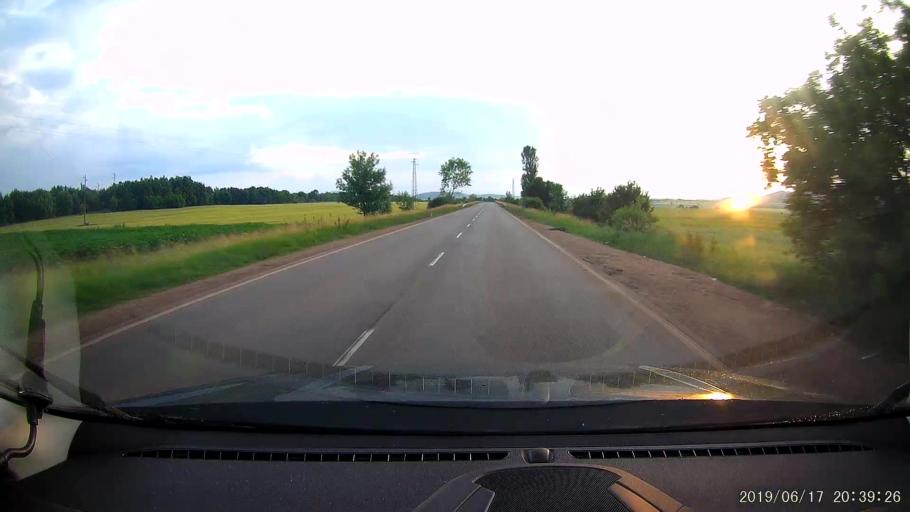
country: BG
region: Sofiya
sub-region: Obshtina Slivnitsa
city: Slivnitsa
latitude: 42.8817
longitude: 23.0069
